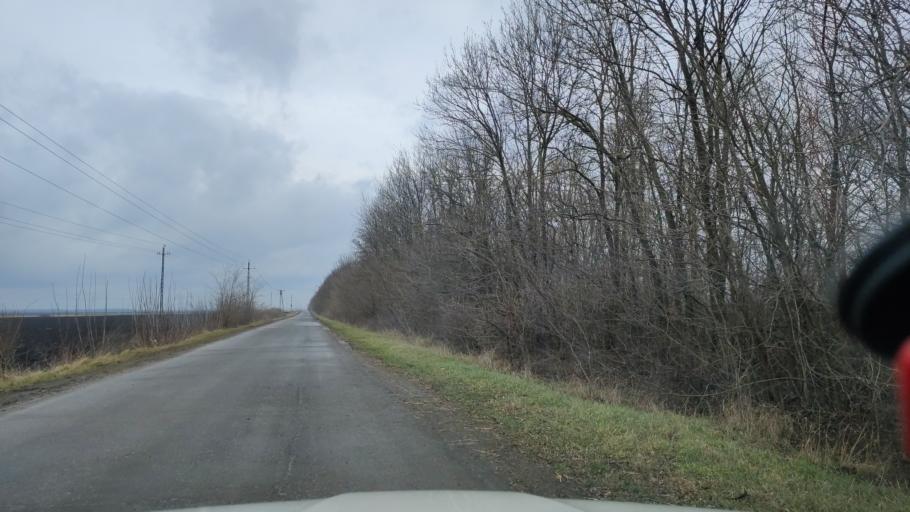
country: HU
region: Hajdu-Bihar
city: Hajduszoboszlo
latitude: 47.4670
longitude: 21.4149
